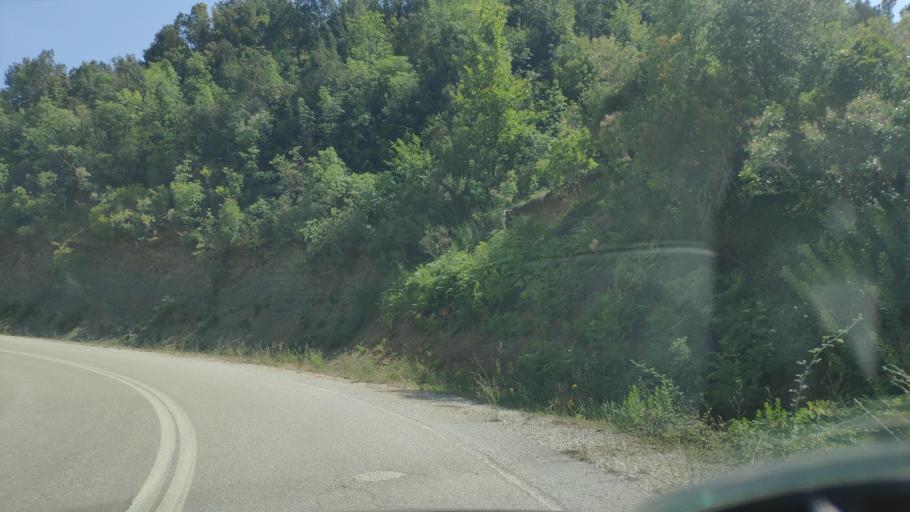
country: GR
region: Epirus
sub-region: Nomos Artas
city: Ano Kalentini
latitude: 39.2271
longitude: 21.1481
